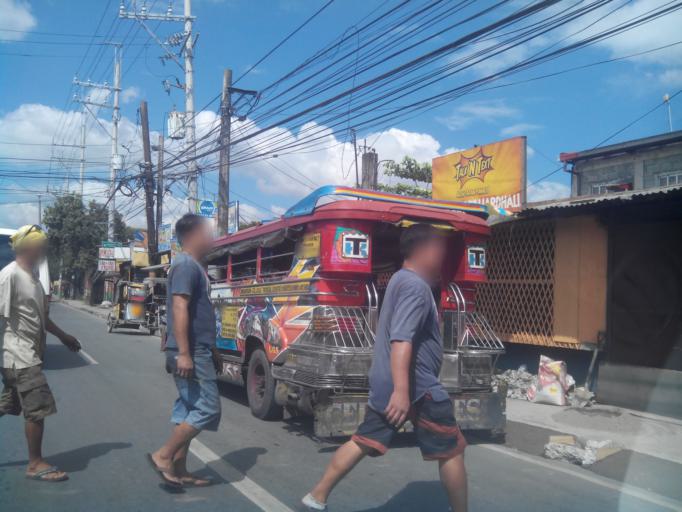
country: PH
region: Calabarzon
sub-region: Province of Rizal
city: Taytay
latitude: 14.5487
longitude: 121.1411
